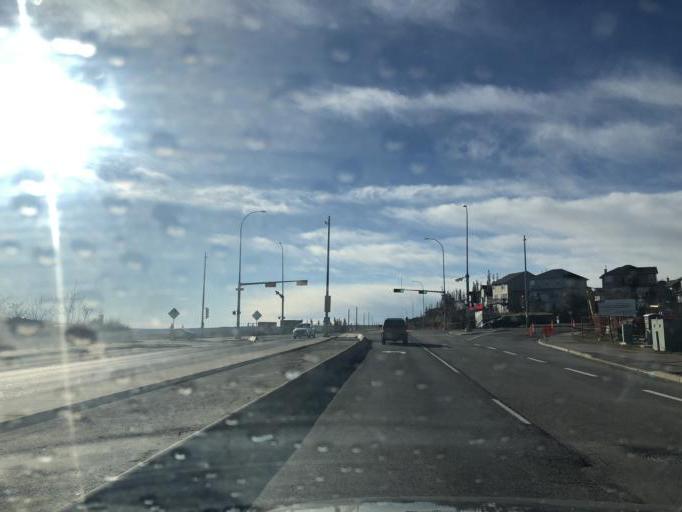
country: CA
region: Alberta
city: Calgary
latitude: 51.0388
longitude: -114.2111
